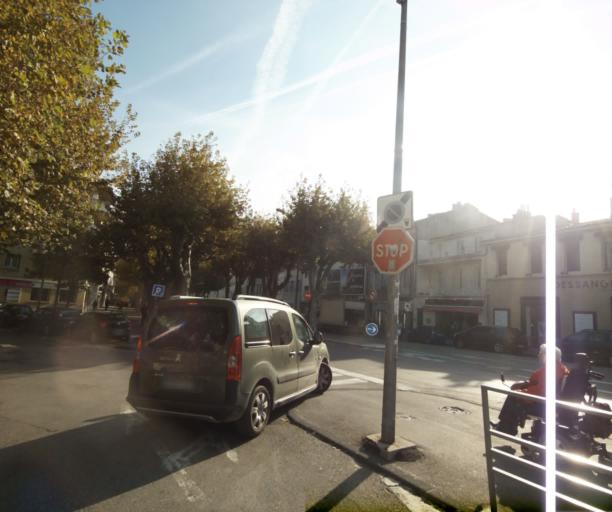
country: FR
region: Provence-Alpes-Cote d'Azur
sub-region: Departement des Bouches-du-Rhone
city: Aubagne
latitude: 43.2927
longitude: 5.5656
